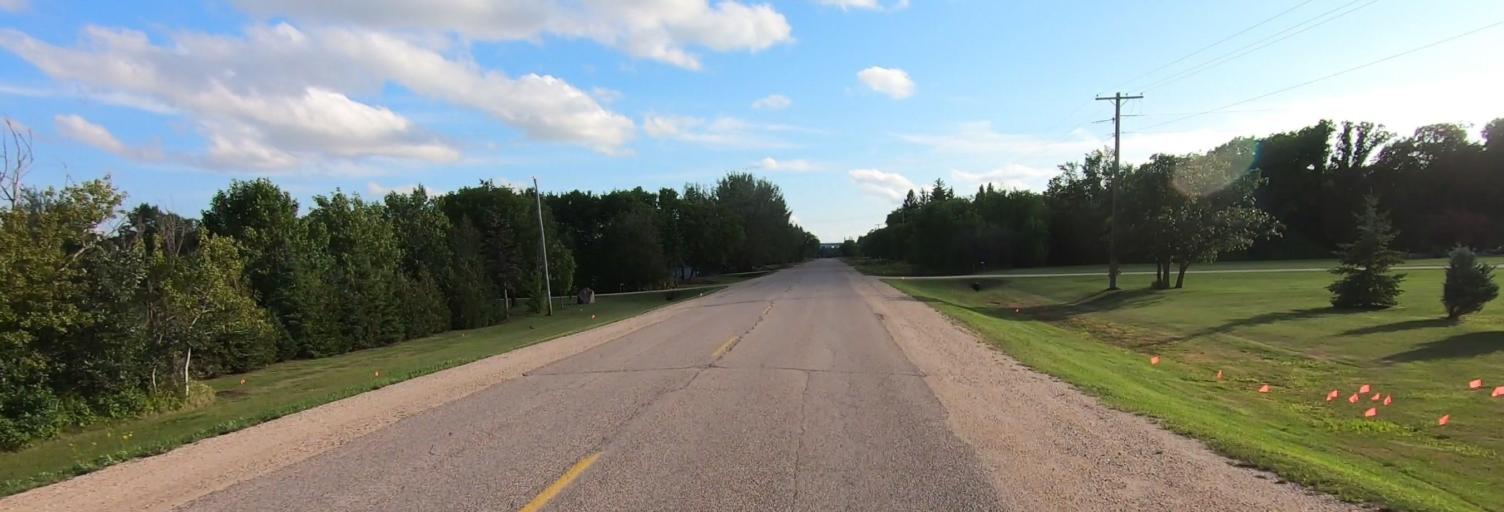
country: CA
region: Manitoba
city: Selkirk
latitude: 50.1984
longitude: -96.8407
